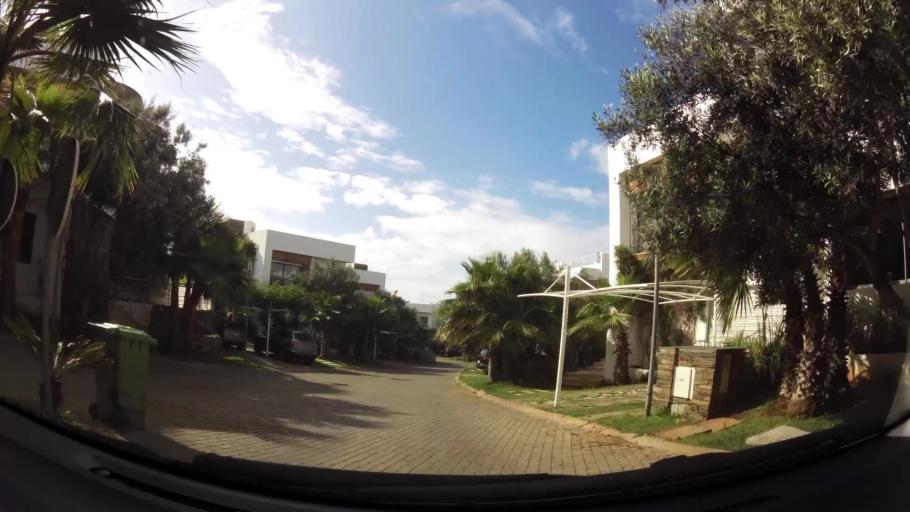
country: MA
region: Grand Casablanca
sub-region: Casablanca
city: Casablanca
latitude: 33.5685
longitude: -7.7050
